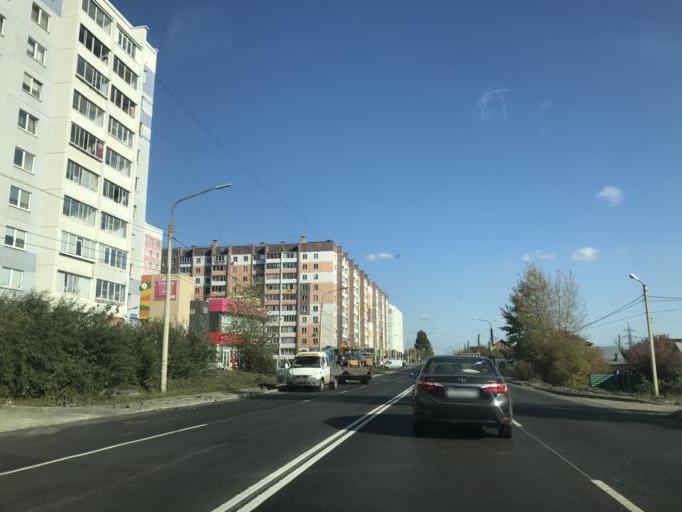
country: RU
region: Chelyabinsk
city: Roshchino
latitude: 55.2346
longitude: 61.3019
